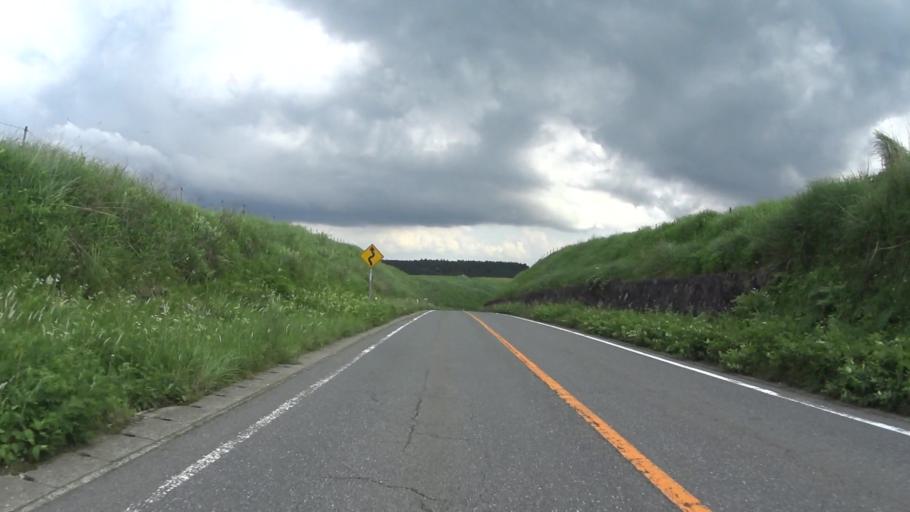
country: JP
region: Kumamoto
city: Aso
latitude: 33.0183
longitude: 131.1526
